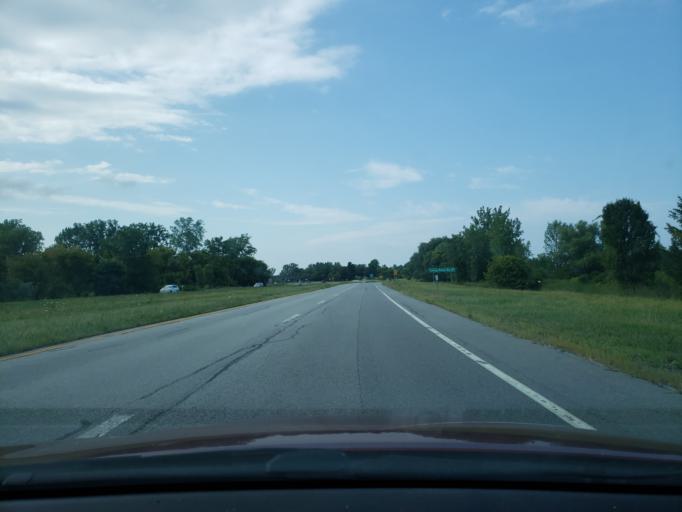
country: US
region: New York
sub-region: Monroe County
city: Greece
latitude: 43.2770
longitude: -77.6929
